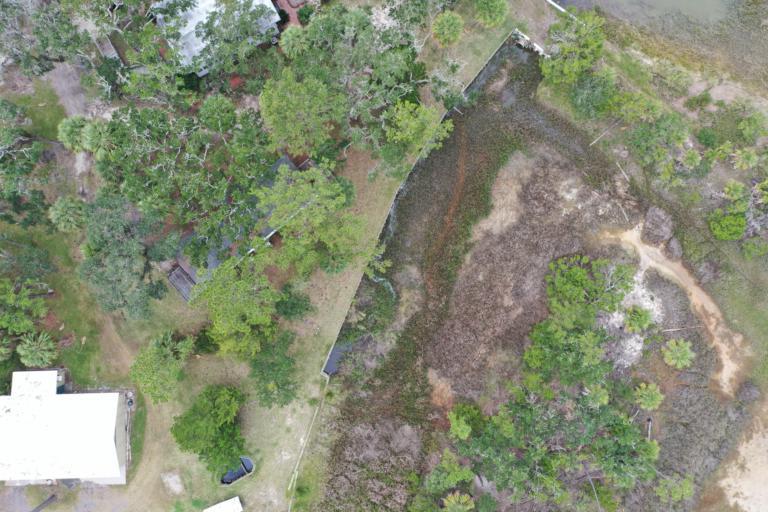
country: US
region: Georgia
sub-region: Chatham County
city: Whitemarsh Island
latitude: 31.9898
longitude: -81.0206
